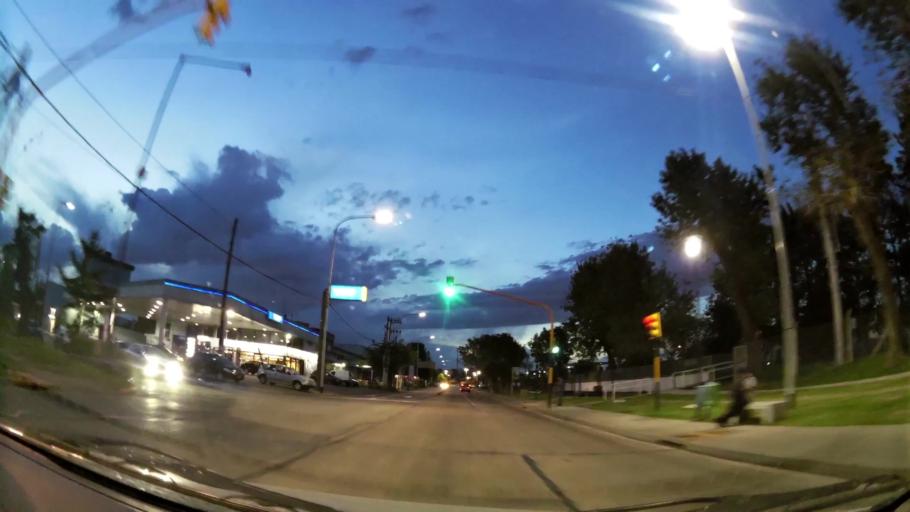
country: AR
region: Buenos Aires
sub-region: Partido de Avellaneda
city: Avellaneda
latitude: -34.6957
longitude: -58.3181
